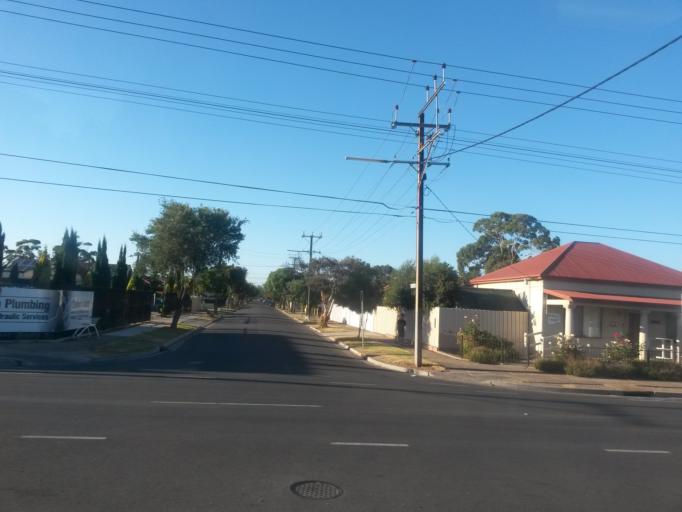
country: AU
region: South Australia
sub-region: Charles Sturt
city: Woodville
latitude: -34.8755
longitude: 138.5615
